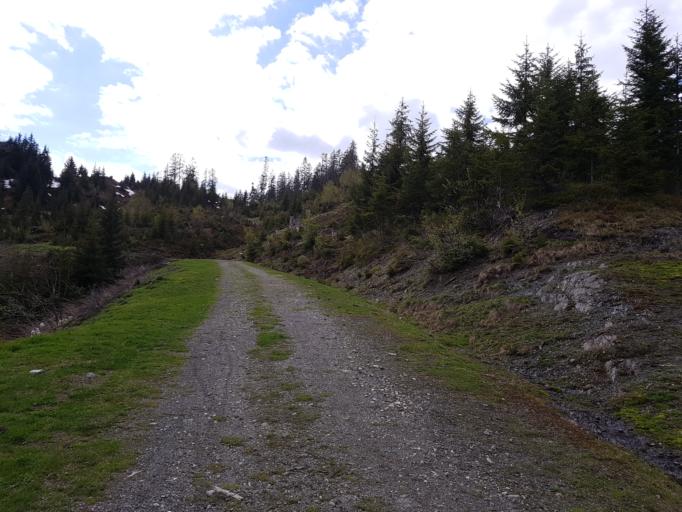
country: AT
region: Salzburg
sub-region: Politischer Bezirk Sankt Johann im Pongau
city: Sankt Veit im Pongau
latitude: 47.3479
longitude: 13.1451
